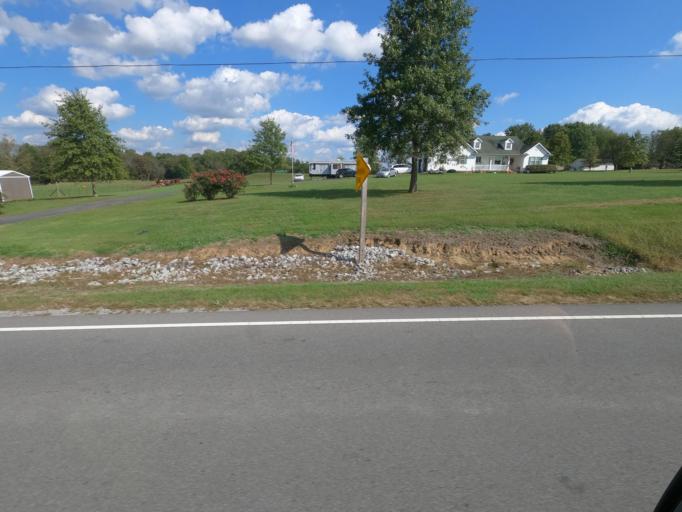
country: US
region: Illinois
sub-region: Massac County
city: Metropolis
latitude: 37.1711
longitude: -88.6767
